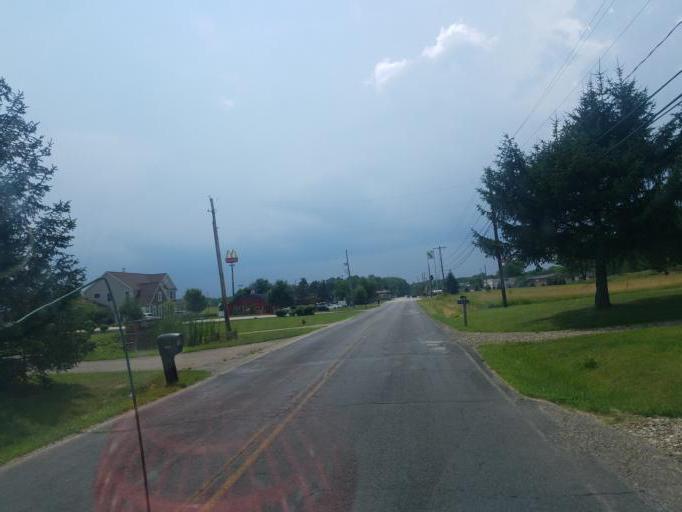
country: US
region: Ohio
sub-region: Portage County
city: Ravenna
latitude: 41.1111
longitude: -81.2384
